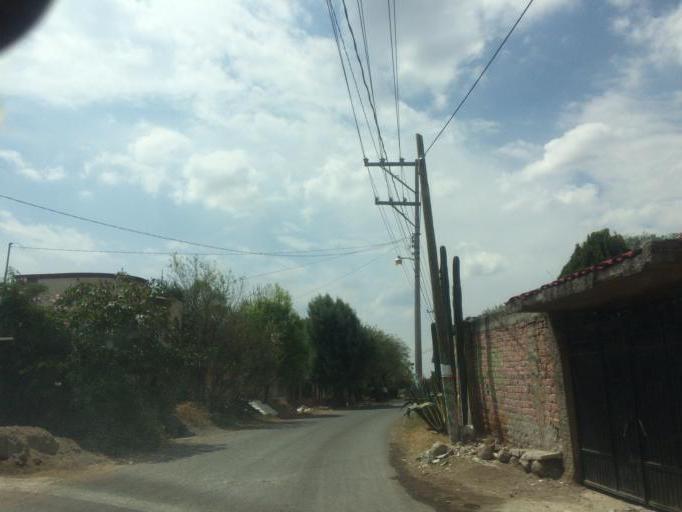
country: MX
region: Guanajuato
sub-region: Silao de la Victoria
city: Colonia Francisco Javier Mina
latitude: 21.0082
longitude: -101.4360
